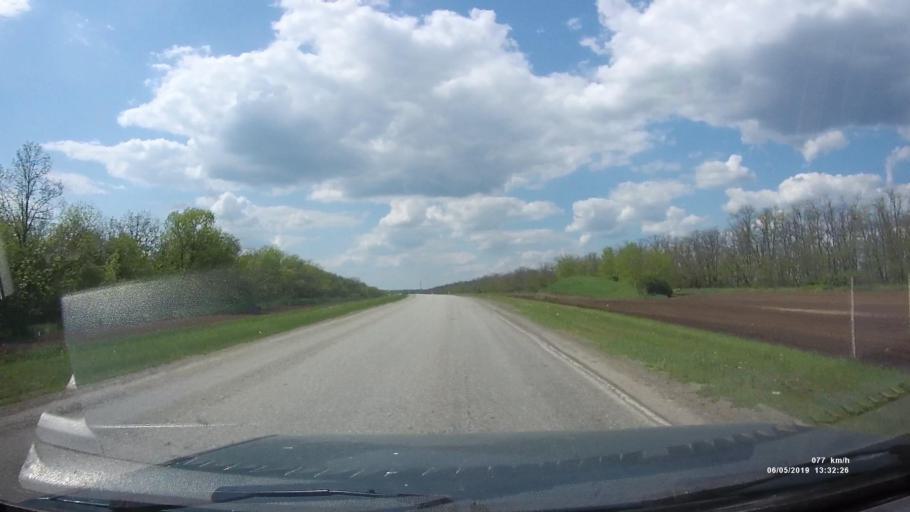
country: RU
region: Rostov
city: Ust'-Donetskiy
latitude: 47.6835
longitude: 40.7958
